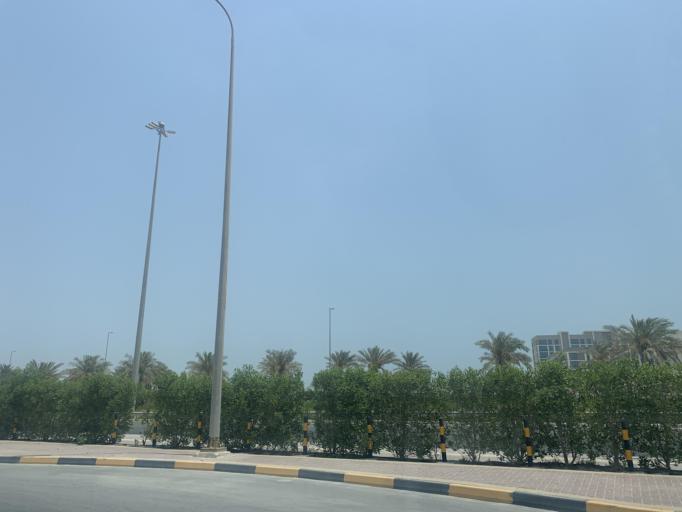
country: BH
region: Muharraq
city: Al Muharraq
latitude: 26.3066
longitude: 50.6393
